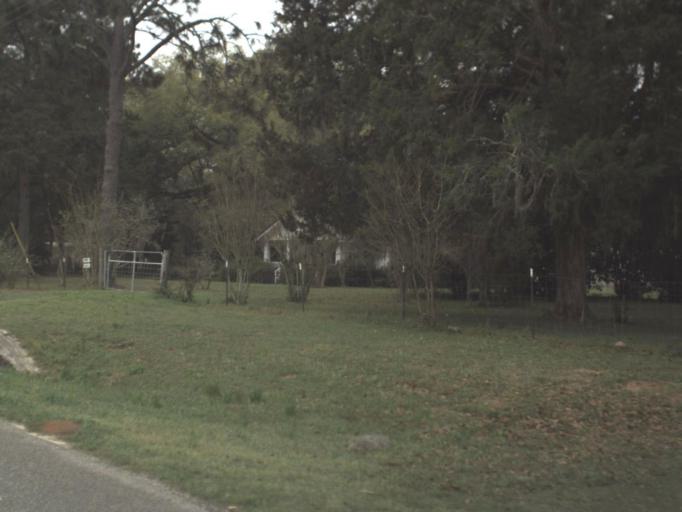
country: US
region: Florida
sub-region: Gadsden County
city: Gretna
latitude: 30.5631
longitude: -84.6766
